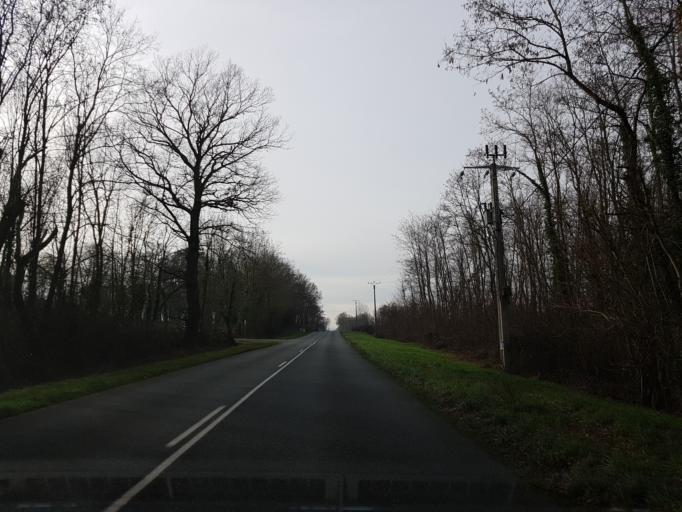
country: FR
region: Auvergne
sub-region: Departement de l'Allier
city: Yzeure
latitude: 46.5754
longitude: 3.3689
